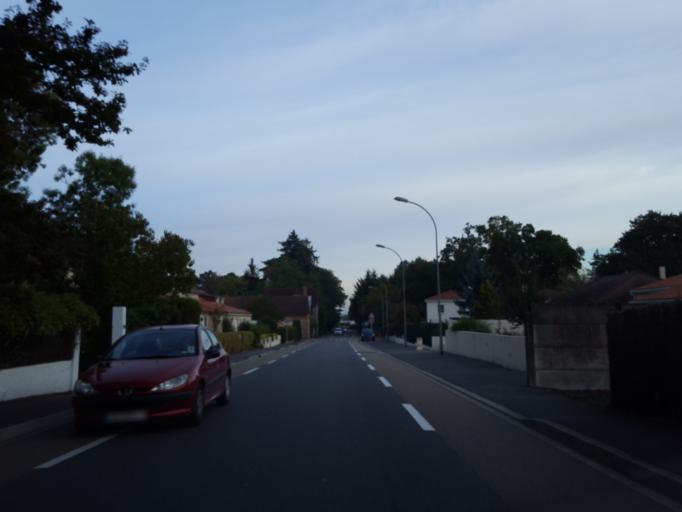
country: FR
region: Pays de la Loire
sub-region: Departement de la Loire-Atlantique
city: Basse-Goulaine
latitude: 47.1987
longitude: -1.4655
